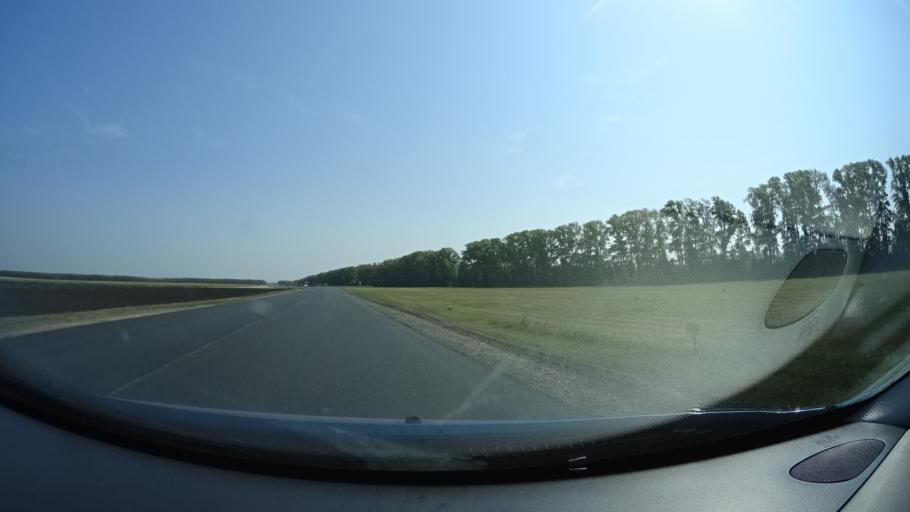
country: RU
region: Bashkortostan
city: Karmaskaly
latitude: 54.3854
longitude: 56.1452
